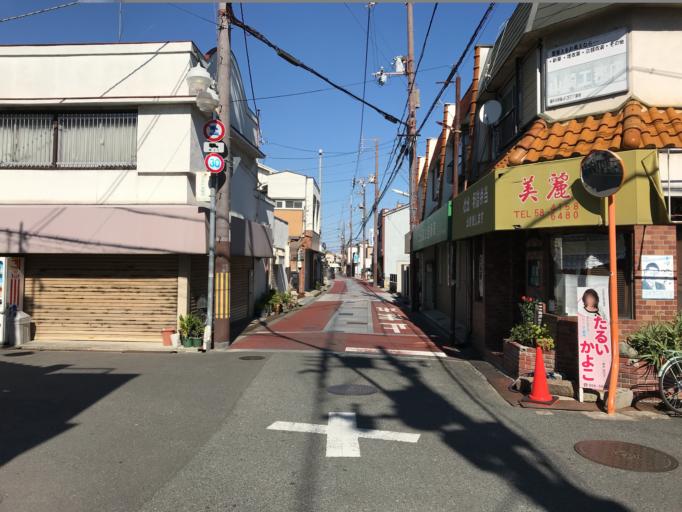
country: JP
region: Osaka
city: Kashihara
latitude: 34.5525
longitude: 135.6118
